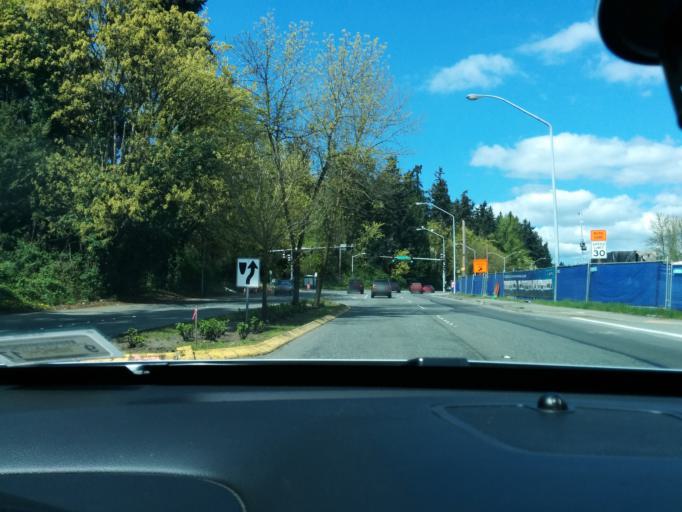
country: US
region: Washington
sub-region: King County
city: Newport
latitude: 47.5853
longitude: -122.1903
